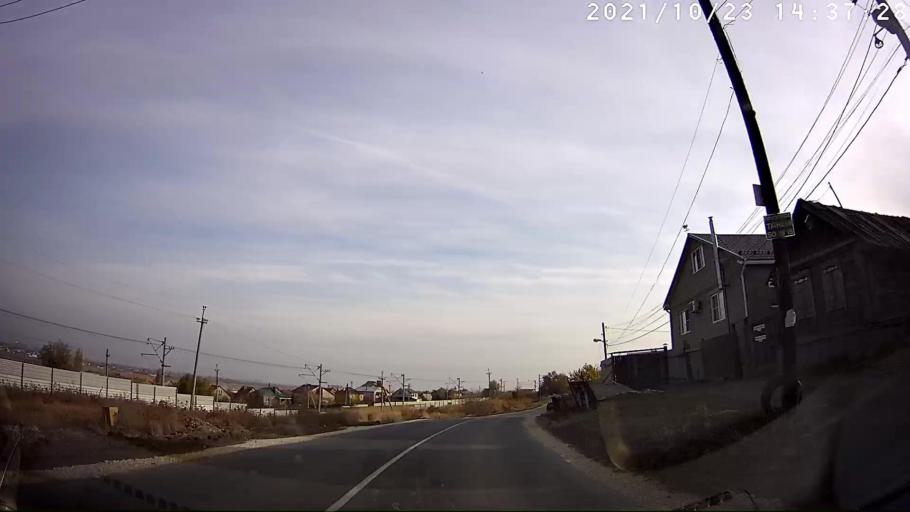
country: RU
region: Volgograd
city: Krasnoslobodsk
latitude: 48.4978
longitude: 44.5488
